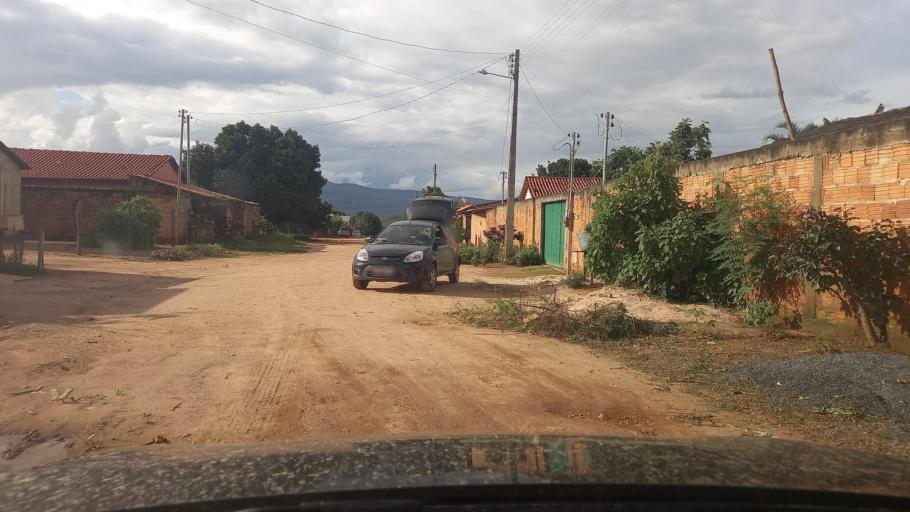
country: BR
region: Goias
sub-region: Cavalcante
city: Cavalcante
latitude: -13.8008
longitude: -47.4432
